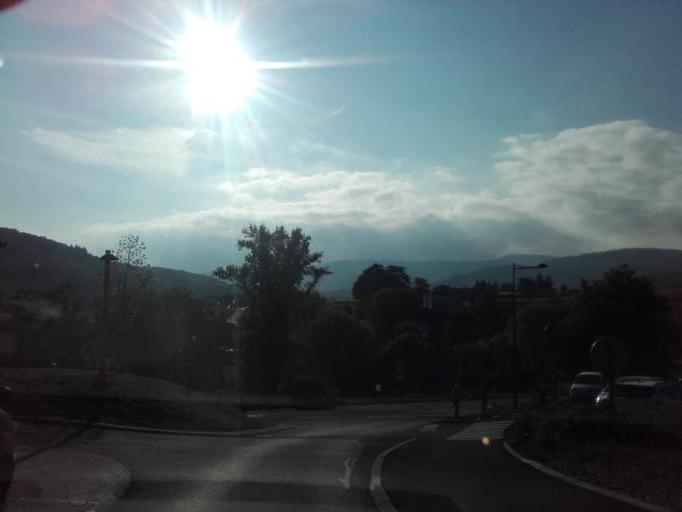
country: FR
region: Rhone-Alpes
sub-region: Departement du Rhone
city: Fleurie
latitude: 46.2356
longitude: 4.7088
